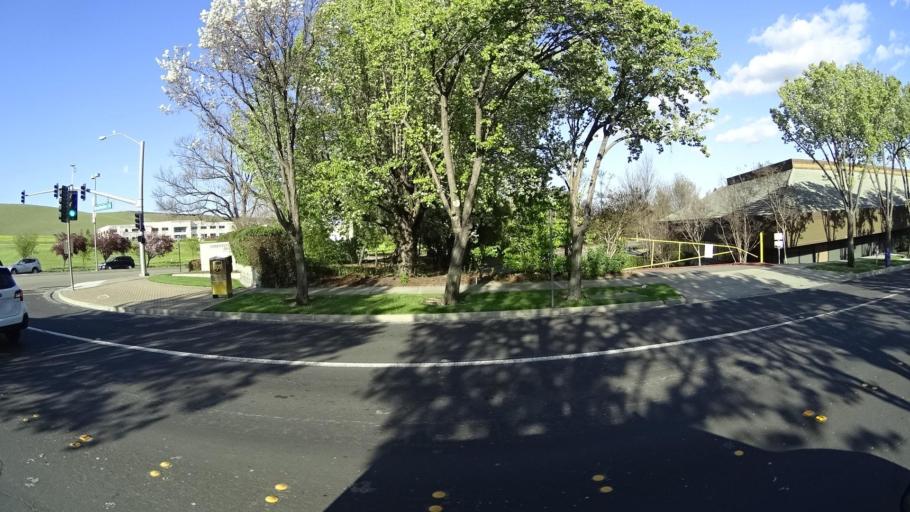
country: US
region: California
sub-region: Alameda County
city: Livermore
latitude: 37.7043
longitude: -121.8169
